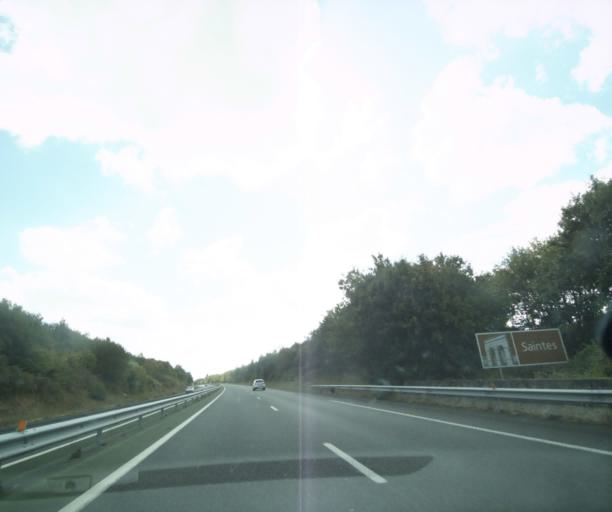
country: FR
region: Poitou-Charentes
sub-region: Departement de la Charente-Maritime
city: Saint-Georges-des-Coteaux
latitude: 45.8051
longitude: -0.6904
